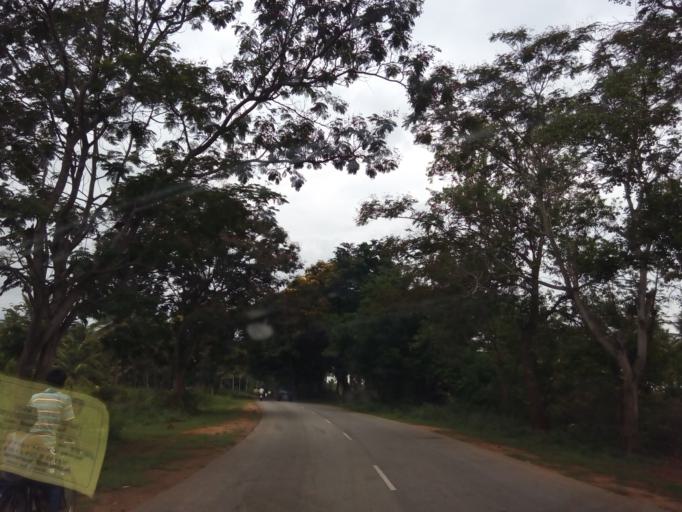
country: IN
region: Karnataka
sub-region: Hassan
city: Shravanabelagola
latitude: 12.8757
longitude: 76.4368
